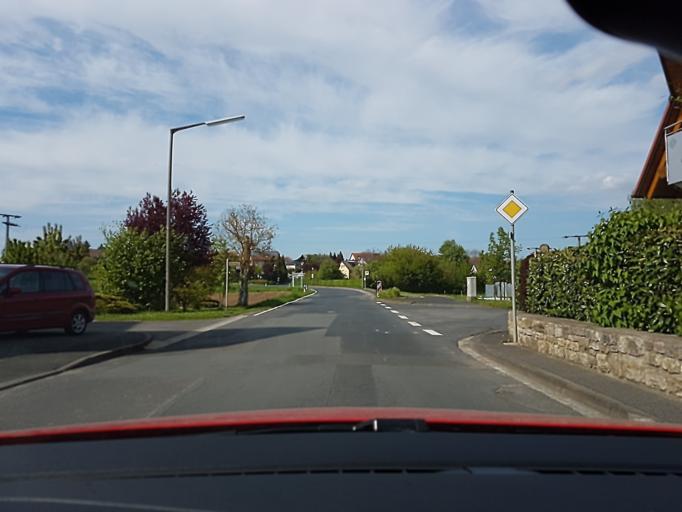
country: DE
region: Bavaria
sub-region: Regierungsbezirk Unterfranken
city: Unterpleichfeld
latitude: 49.8739
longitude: 10.0270
